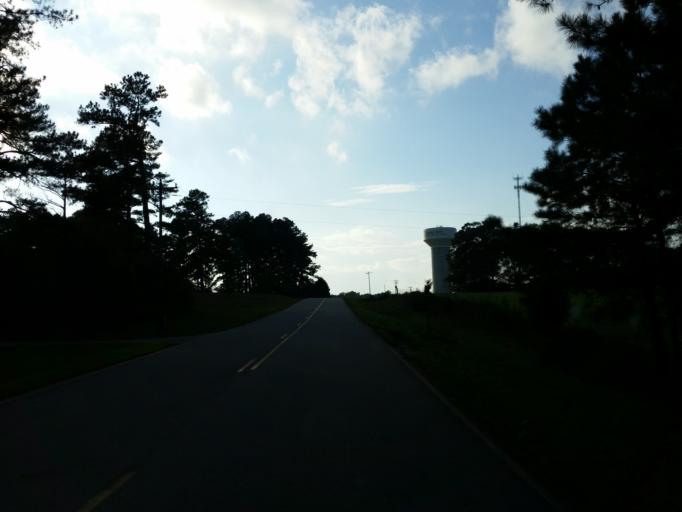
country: US
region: Georgia
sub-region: Monroe County
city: Forsyth
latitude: 32.9786
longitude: -83.8666
